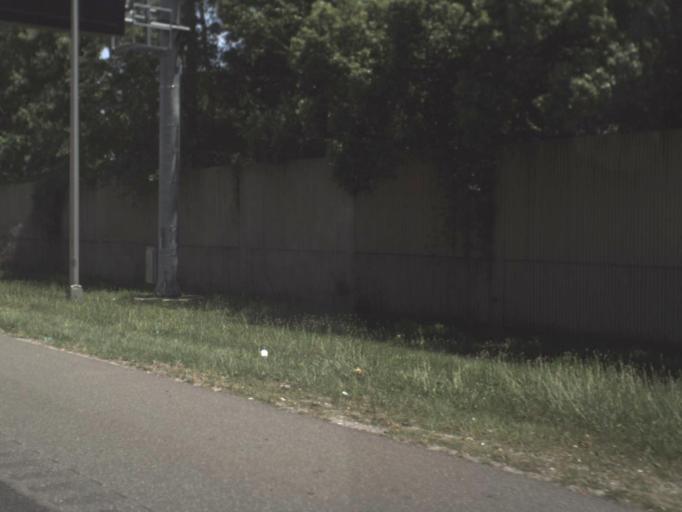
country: US
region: Florida
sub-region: Clay County
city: Orange Park
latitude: 30.1912
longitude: -81.6949
